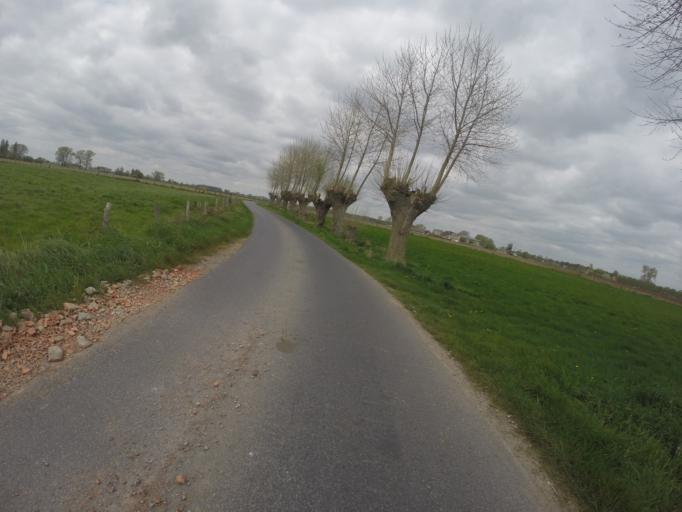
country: BE
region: Flanders
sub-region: Provincie Oost-Vlaanderen
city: Aalter
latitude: 51.0219
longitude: 3.4641
